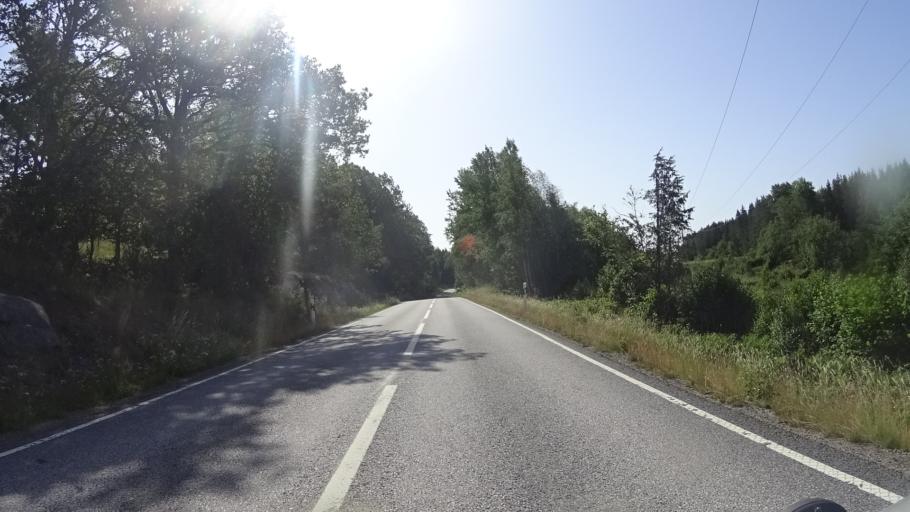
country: SE
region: Kalmar
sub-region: Vasterviks Kommun
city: Overum
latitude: 58.0446
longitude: 16.2158
